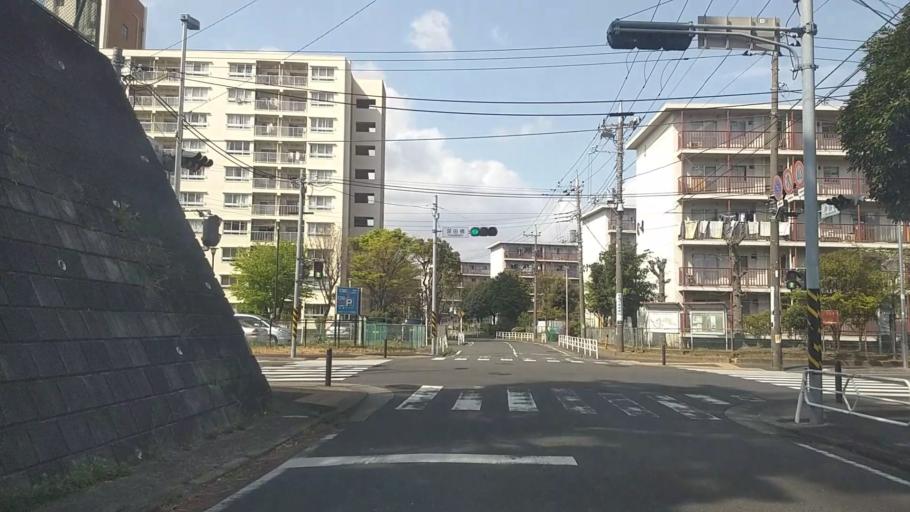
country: JP
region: Kanagawa
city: Kamakura
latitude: 35.3856
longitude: 139.5687
